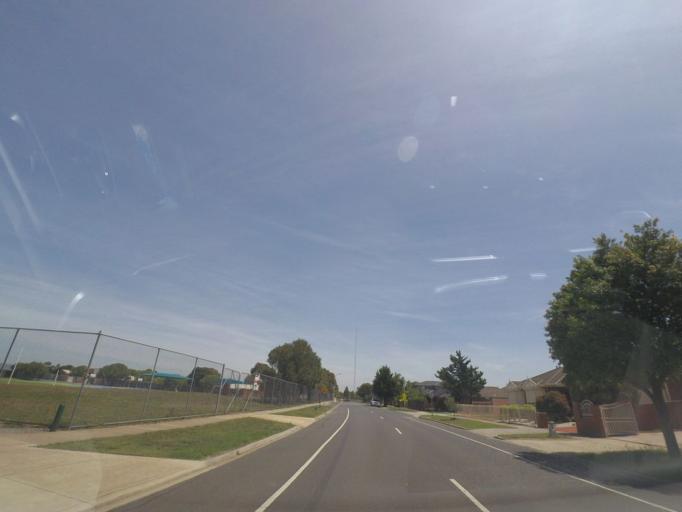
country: AU
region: Victoria
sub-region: Brimbank
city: Keilor Downs
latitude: -37.7160
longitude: 144.7937
